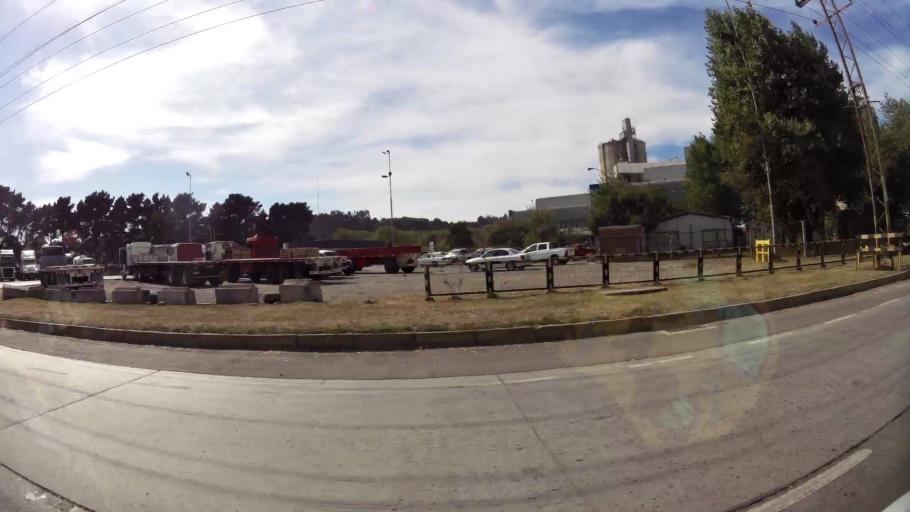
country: CL
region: Biobio
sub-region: Provincia de Concepcion
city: Talcahuano
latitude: -36.7417
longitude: -73.1195
